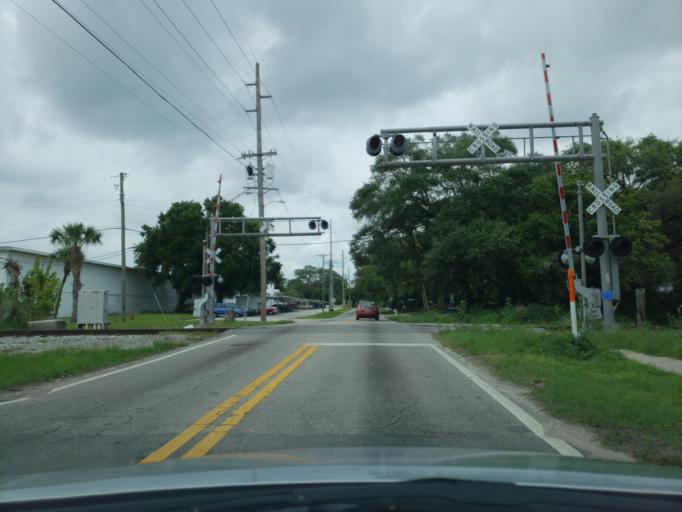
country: US
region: Florida
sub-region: Hillsborough County
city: Temple Terrace
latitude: 28.0034
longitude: -82.4295
